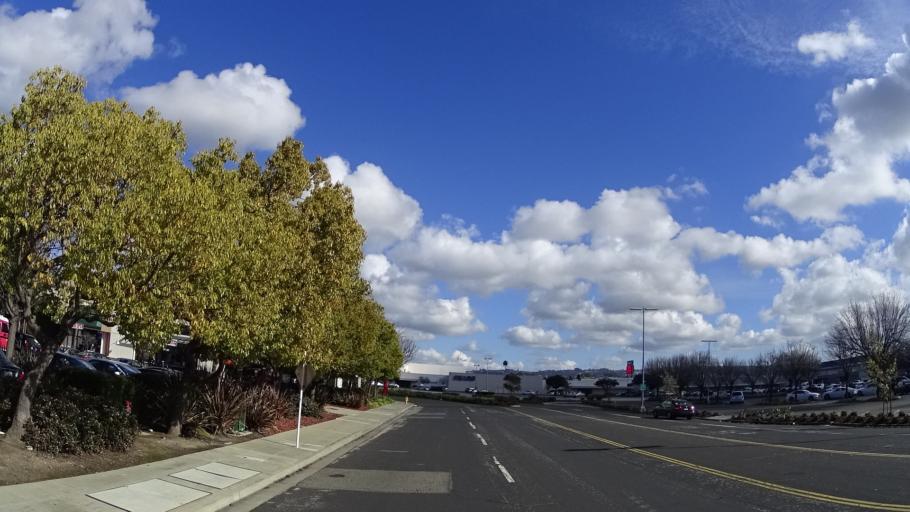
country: US
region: California
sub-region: Alameda County
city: Cherryland
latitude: 37.6522
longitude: -122.1048
